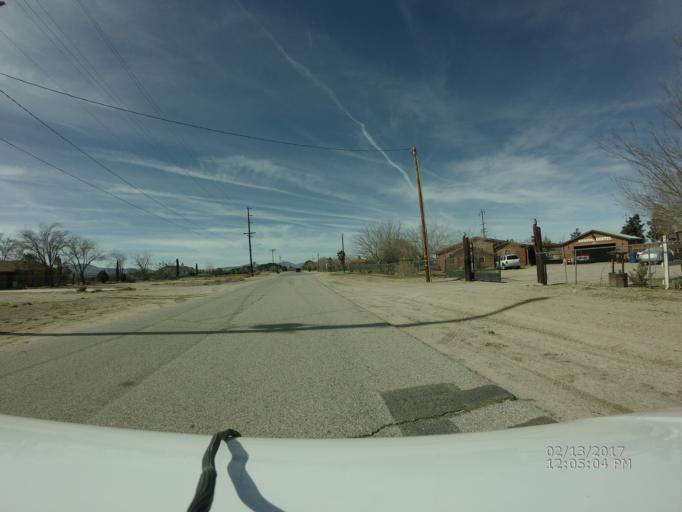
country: US
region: California
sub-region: Los Angeles County
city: Littlerock
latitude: 34.5580
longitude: -117.9333
